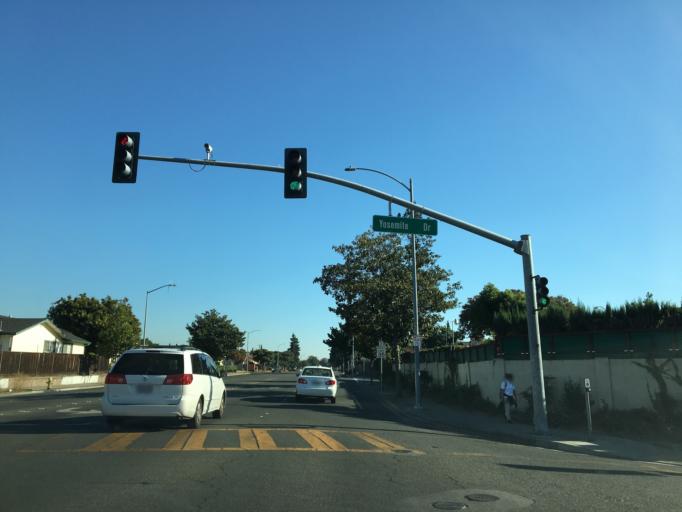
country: US
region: California
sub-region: Santa Clara County
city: Milpitas
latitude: 37.4270
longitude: -121.8810
